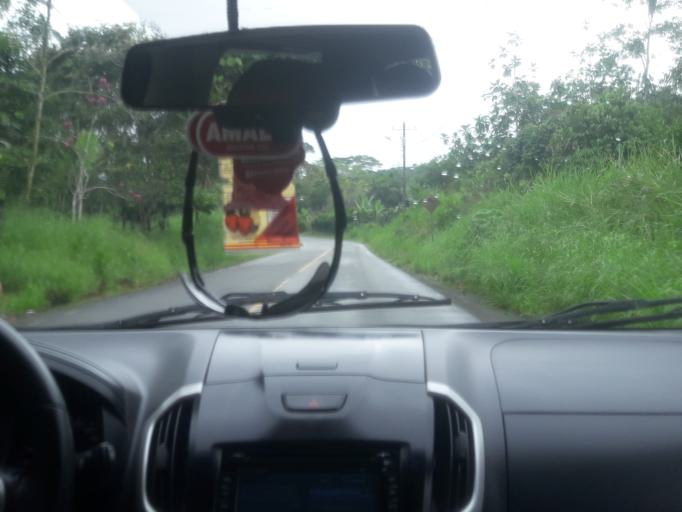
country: EC
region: Napo
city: Tena
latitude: -1.0336
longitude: -77.6856
